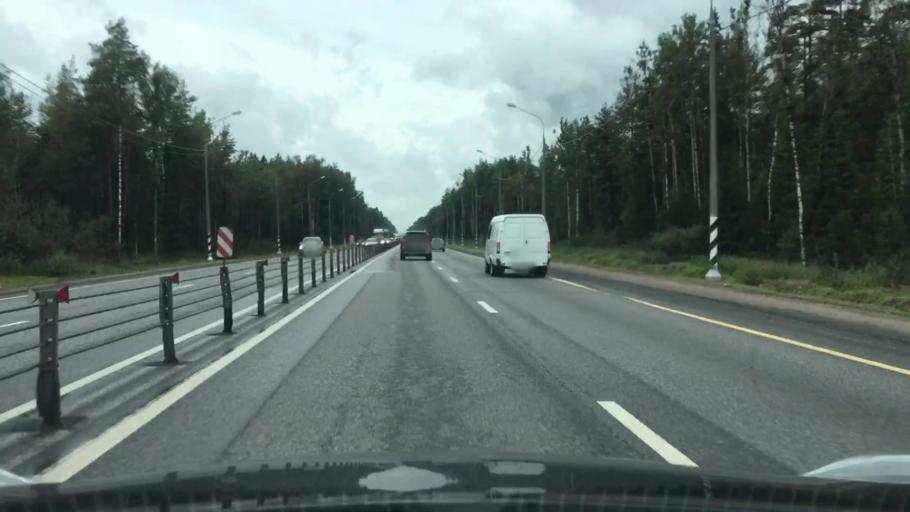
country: RU
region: Moskovskaya
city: Reshetnikovo
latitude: 56.4157
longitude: 36.6377
